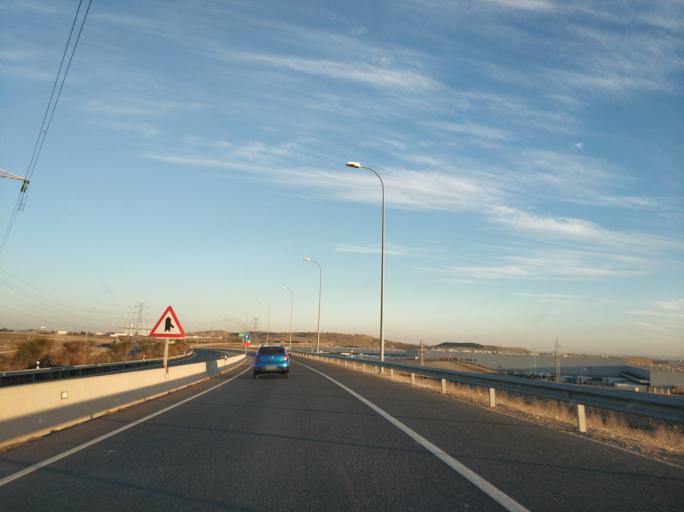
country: ES
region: Madrid
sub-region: Provincia de Madrid
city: Pinto
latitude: 40.2213
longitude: -3.6773
